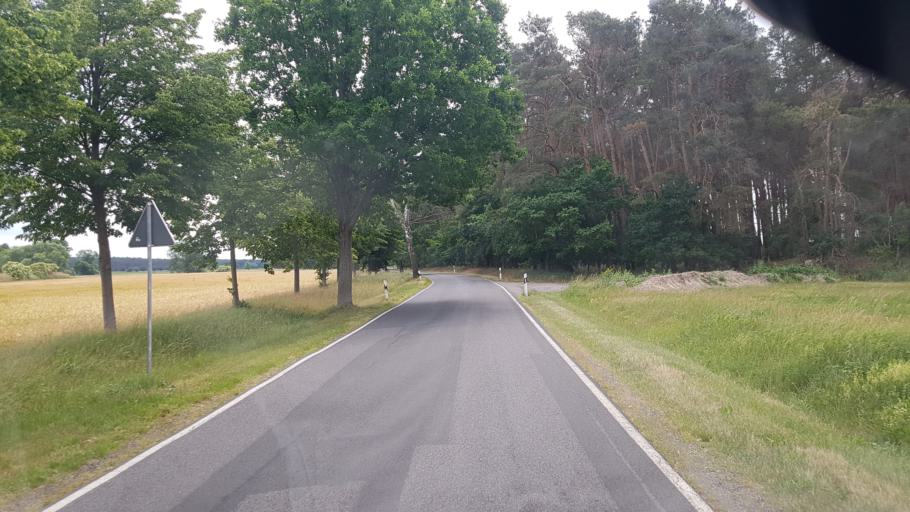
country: DE
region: Brandenburg
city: Ihlow
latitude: 51.8273
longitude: 13.2360
